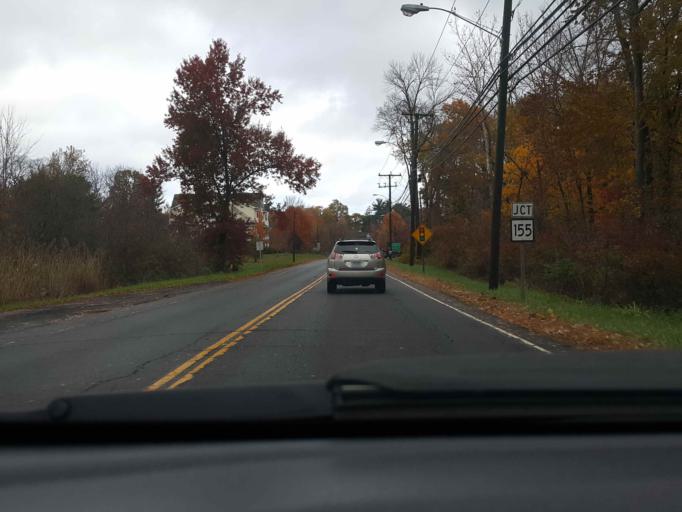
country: US
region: Connecticut
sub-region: Middlesex County
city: Middletown
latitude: 41.5298
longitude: -72.6614
